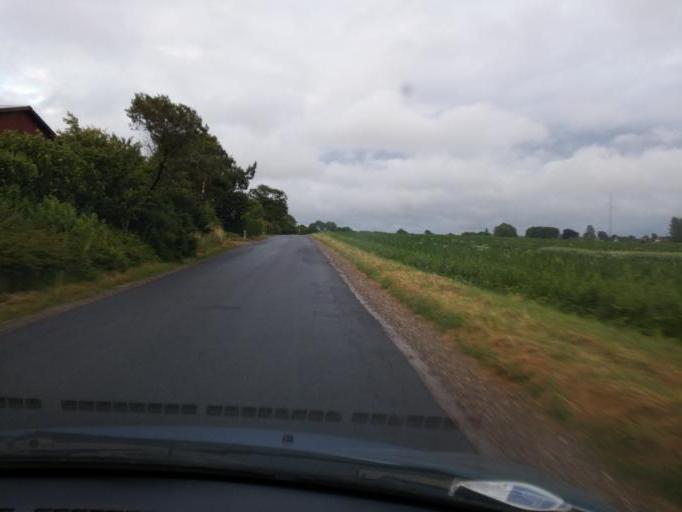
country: DK
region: South Denmark
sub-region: Kerteminde Kommune
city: Kerteminde
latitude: 55.5041
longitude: 10.6403
